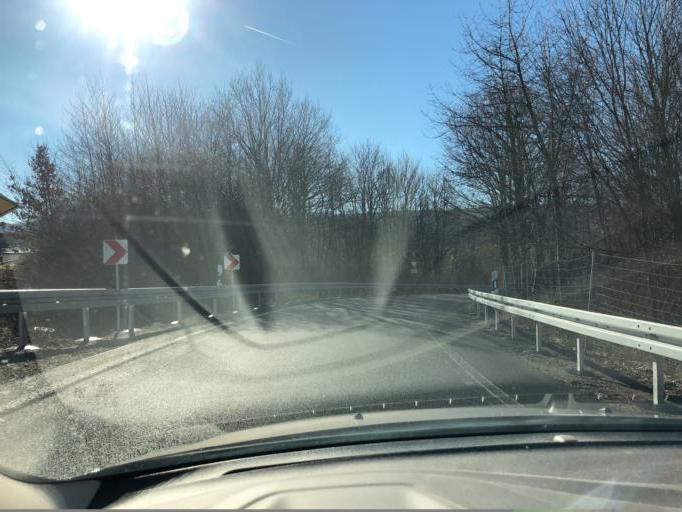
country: DE
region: Lower Saxony
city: Bad Harzburg
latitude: 51.9096
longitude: 10.5536
